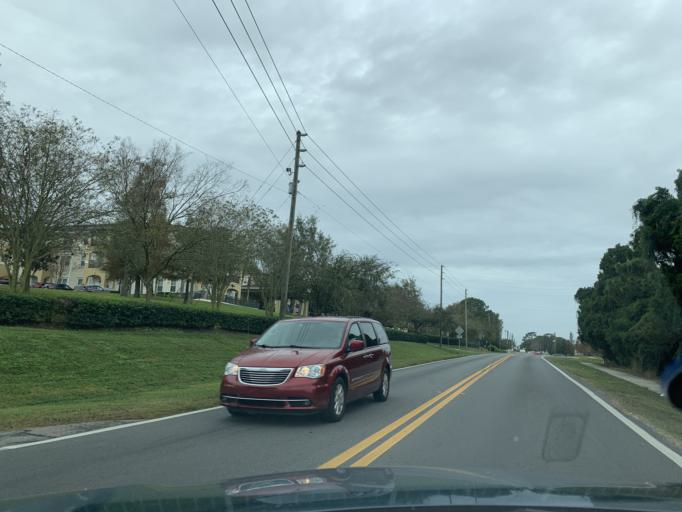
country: US
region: Florida
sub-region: Pasco County
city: Zephyrhills North
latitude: 28.2665
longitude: -82.1841
